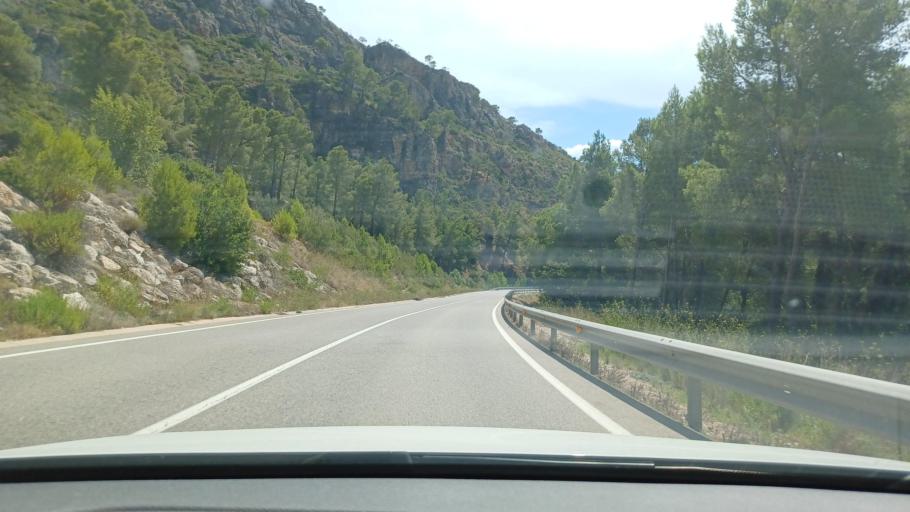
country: ES
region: Catalonia
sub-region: Provincia de Tarragona
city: Benifallet
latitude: 40.9637
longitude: 0.4479
